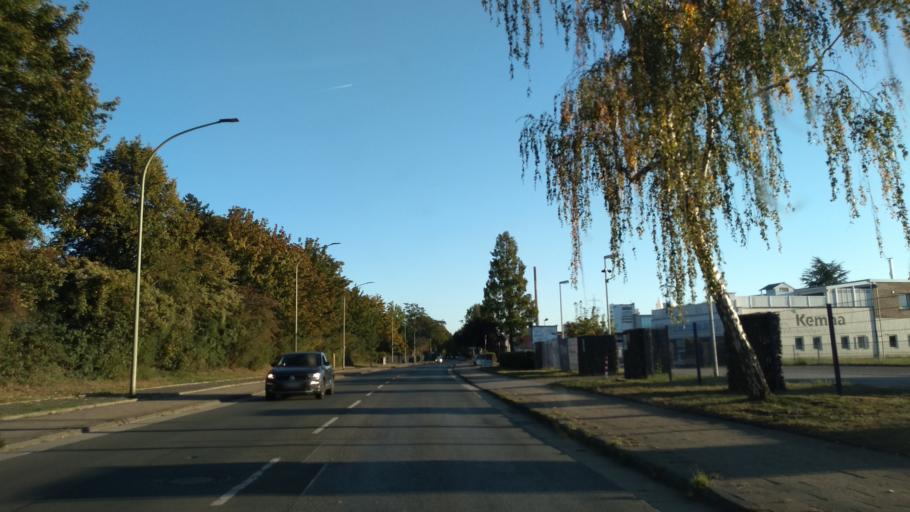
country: DE
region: North Rhine-Westphalia
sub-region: Regierungsbezirk Dusseldorf
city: Dinslaken
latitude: 51.5501
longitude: 6.7135
